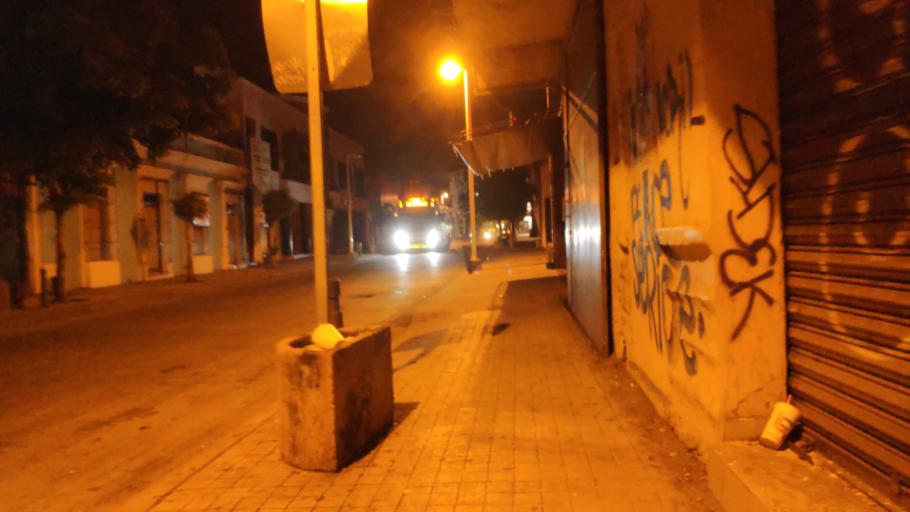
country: MX
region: Sinaloa
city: Culiacan
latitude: 24.8085
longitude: -107.3999
